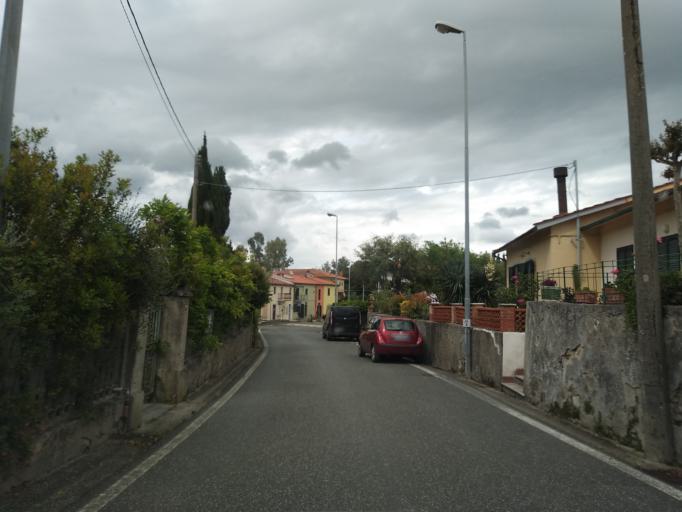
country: IT
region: Tuscany
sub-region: Provincia di Livorno
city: Collesalvetti
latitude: 43.5376
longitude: 10.4419
